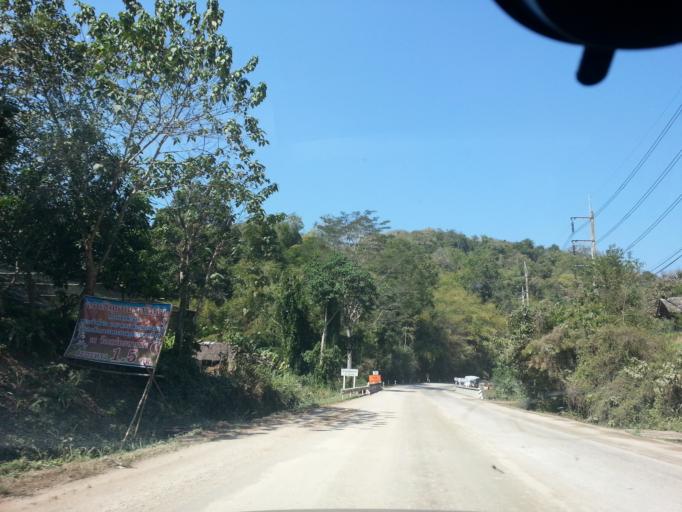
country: TH
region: Chiang Mai
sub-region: Amphoe Chiang Dao
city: Chiang Dao
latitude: 19.2628
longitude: 98.9693
